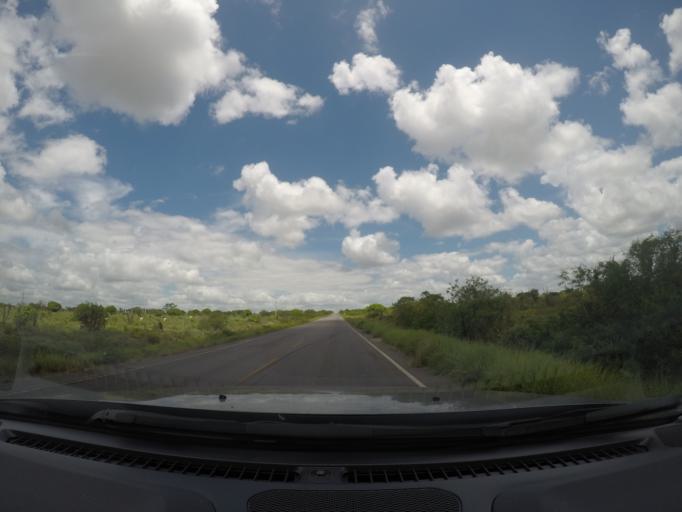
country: BR
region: Bahia
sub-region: Itaberaba
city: Itaberaba
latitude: -12.3544
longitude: -40.0233
